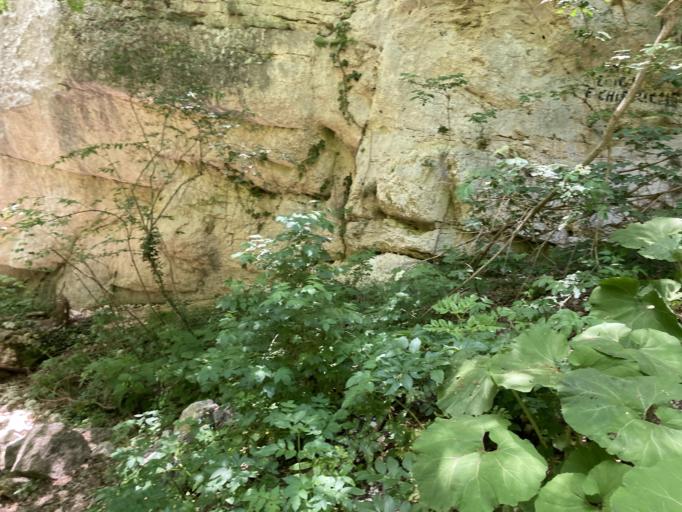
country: IT
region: Abruzzo
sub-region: Provincia dell' Aquila
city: Aielli
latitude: 42.1170
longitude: 13.5712
